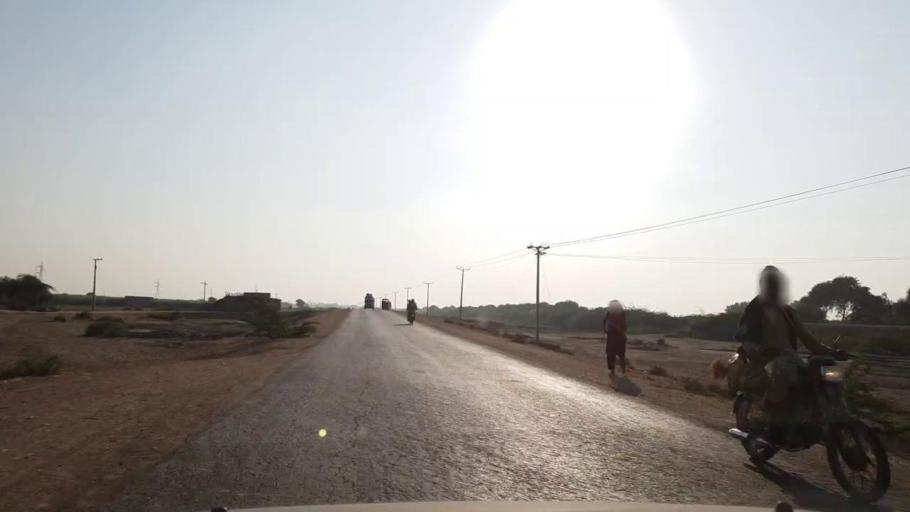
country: PK
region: Sindh
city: Mirpur Batoro
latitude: 24.7575
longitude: 68.2711
